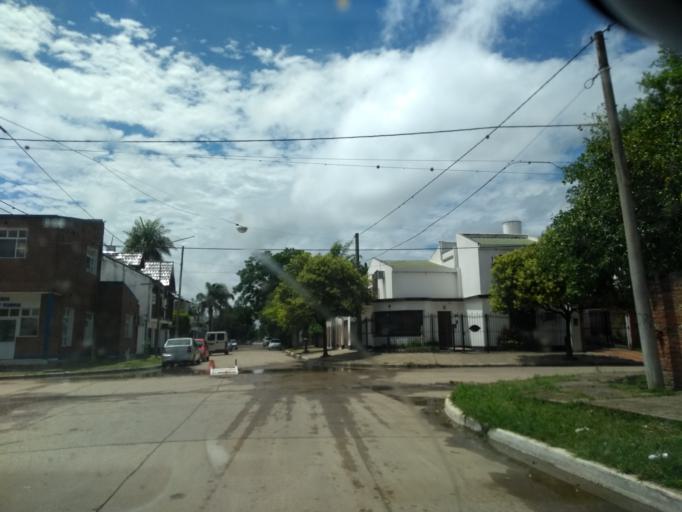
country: AR
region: Chaco
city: Barranqueras
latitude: -27.4783
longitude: -58.9547
